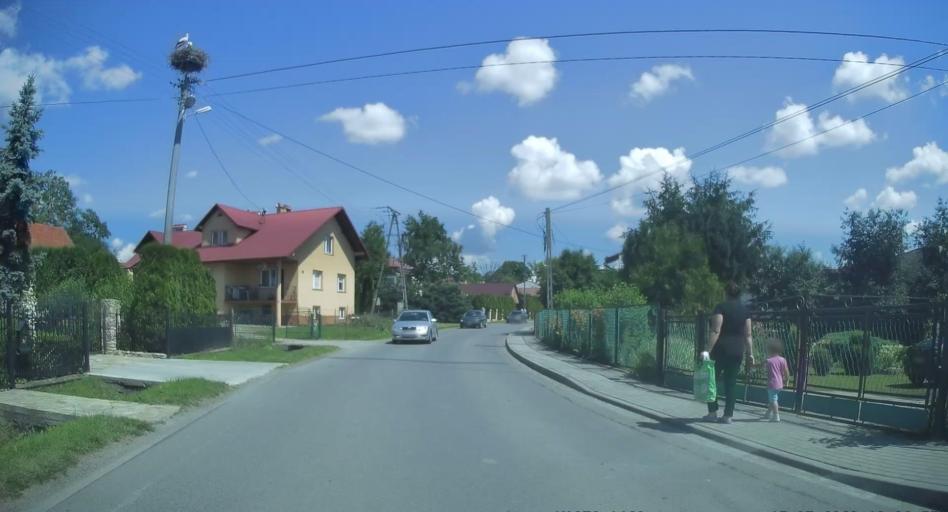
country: PL
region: Subcarpathian Voivodeship
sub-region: Powiat przemyski
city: Medyka
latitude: 49.8234
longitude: 22.8660
